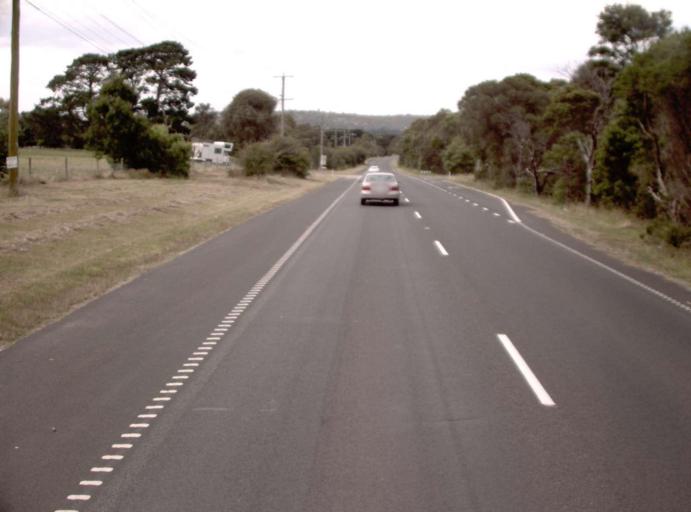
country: AU
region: Victoria
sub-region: Mornington Peninsula
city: Moorooduc
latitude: -38.2390
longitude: 145.0861
